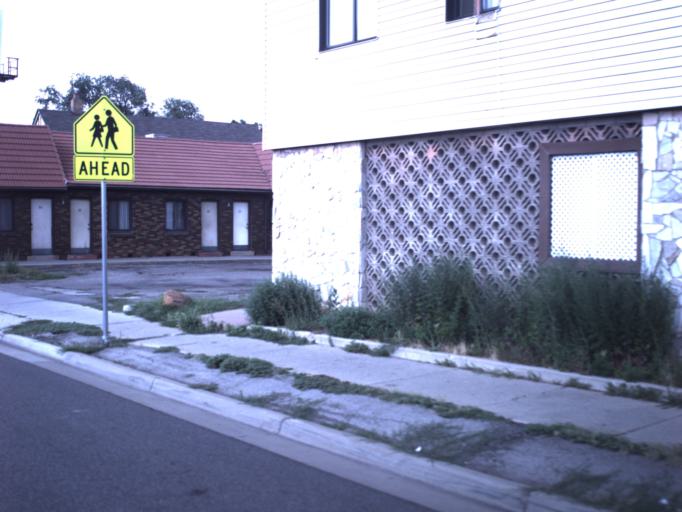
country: US
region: Utah
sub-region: Salt Lake County
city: South Salt Lake
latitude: 40.7323
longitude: -111.8881
